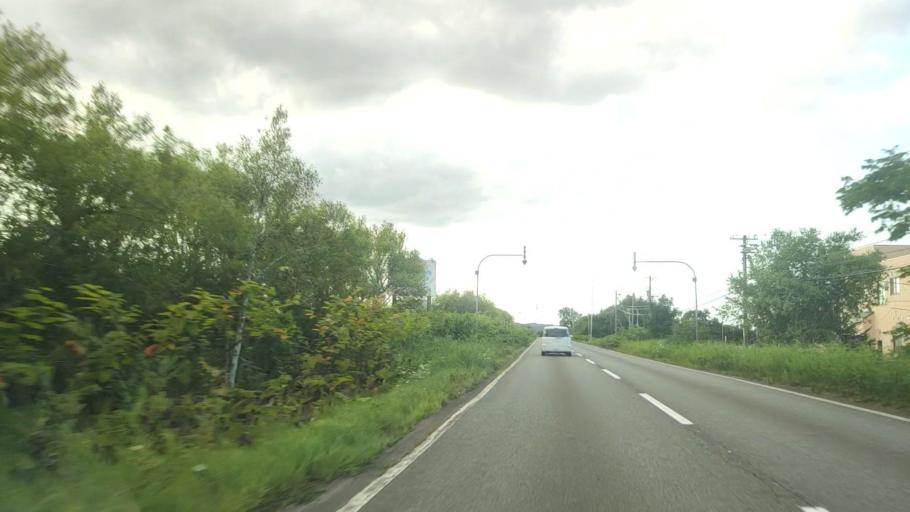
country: JP
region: Hokkaido
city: Makubetsu
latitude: 45.0018
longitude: 141.8157
